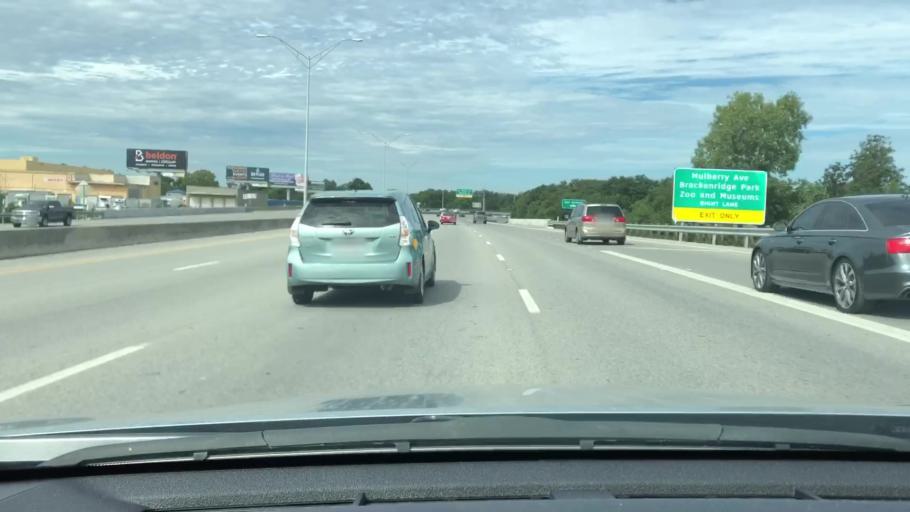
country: US
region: Texas
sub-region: Bexar County
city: San Antonio
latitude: 29.4471
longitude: -98.4794
